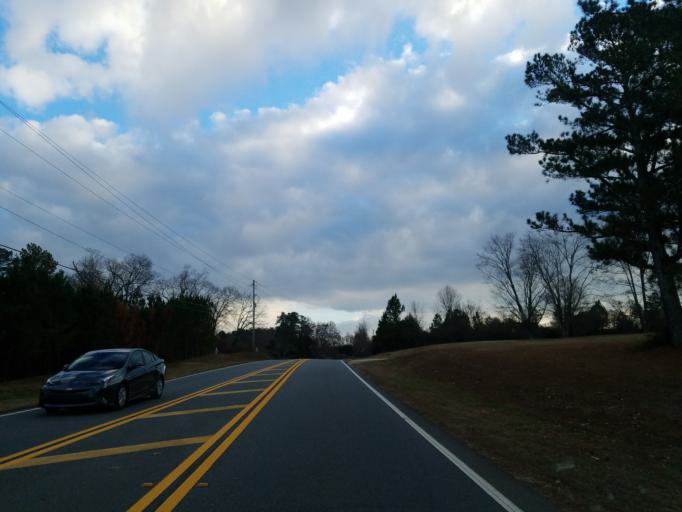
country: US
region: Georgia
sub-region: Forsyth County
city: Cumming
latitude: 34.3062
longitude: -84.0809
